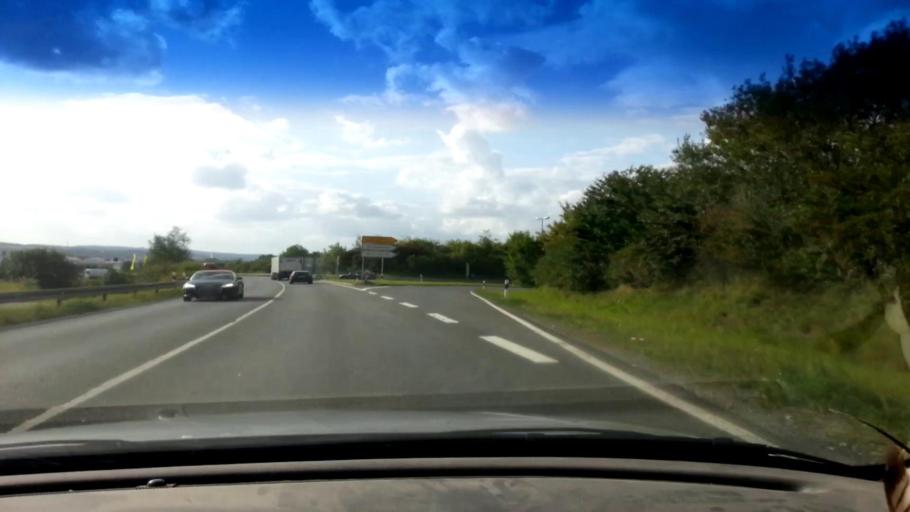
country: DE
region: Bavaria
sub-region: Upper Franconia
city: Himmelkron
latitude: 50.0544
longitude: 11.6277
